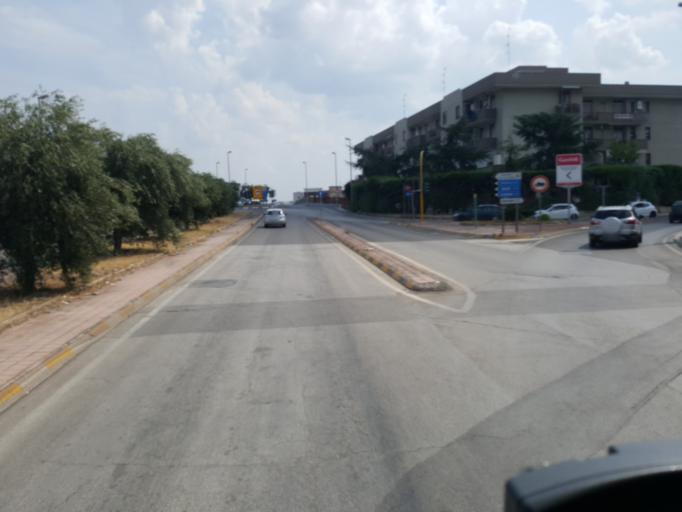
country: IT
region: Apulia
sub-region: Provincia di Bari
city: Modugno
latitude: 41.0907
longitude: 16.7783
